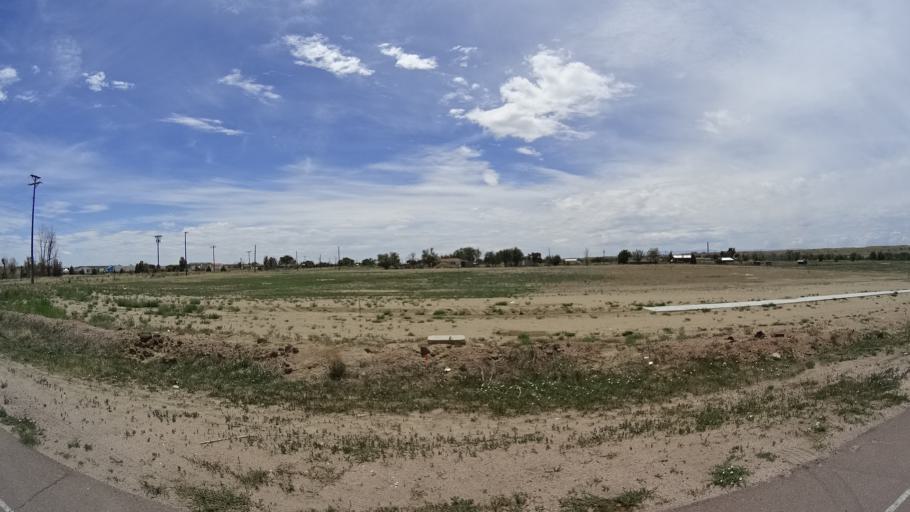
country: US
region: Colorado
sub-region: El Paso County
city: Fountain
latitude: 38.6647
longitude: -104.6862
